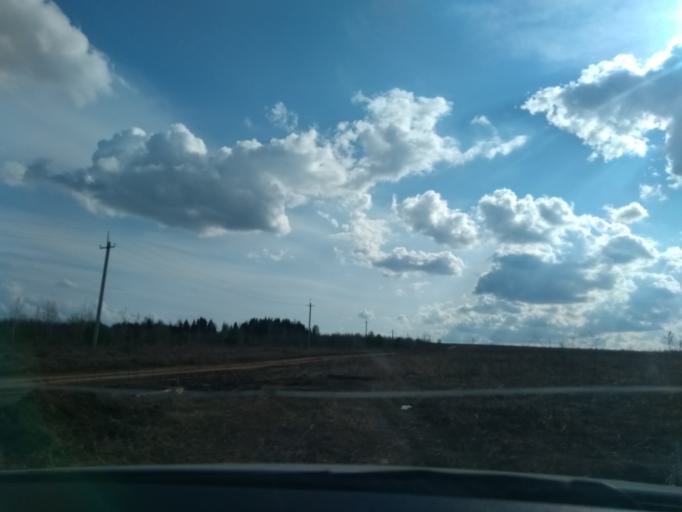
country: RU
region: Perm
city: Sylva
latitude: 57.8407
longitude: 56.7902
